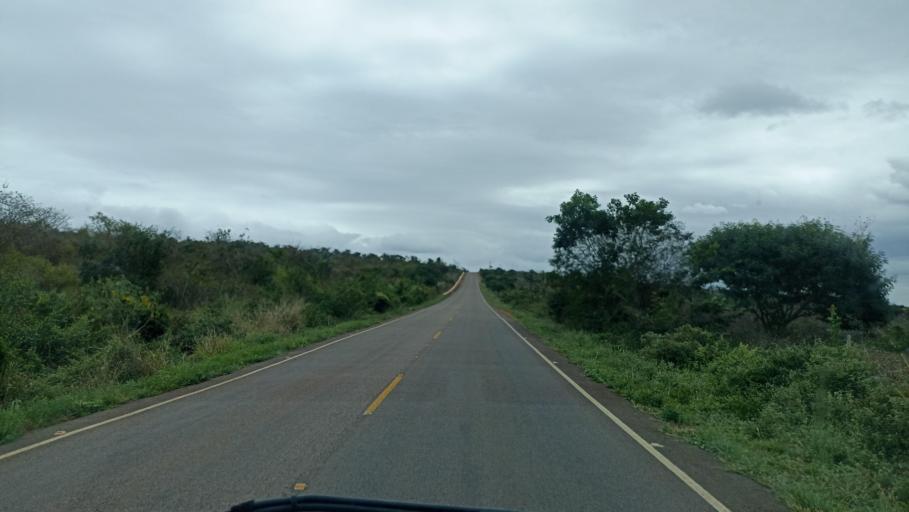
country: BR
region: Bahia
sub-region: Andarai
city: Vera Cruz
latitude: -12.9993
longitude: -40.9924
